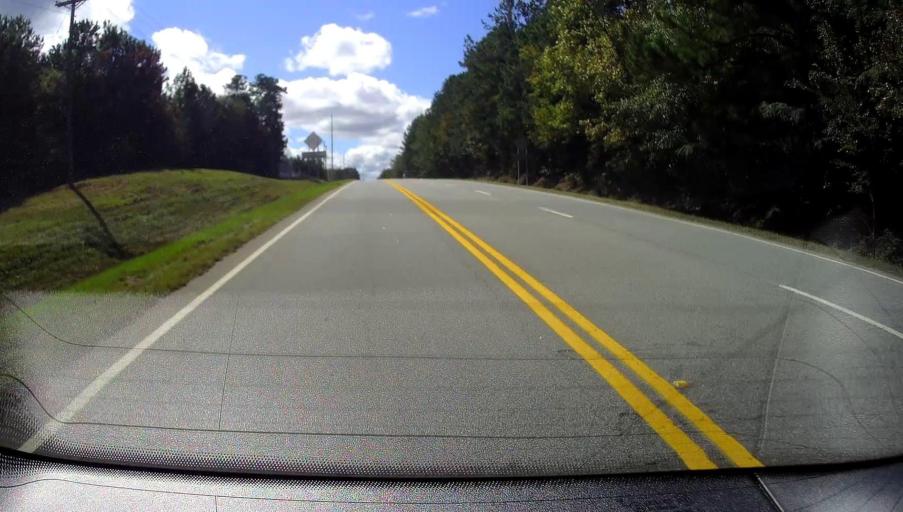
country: US
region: Georgia
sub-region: Jones County
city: Gray
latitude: 32.9292
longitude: -83.5035
